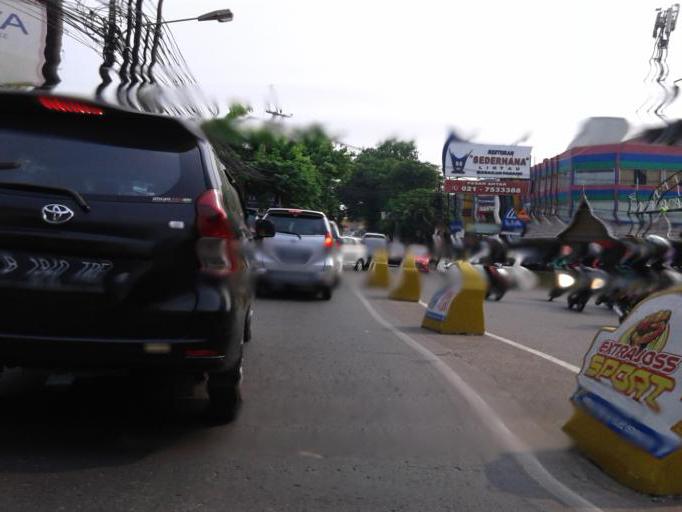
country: ID
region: West Java
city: Pamulang
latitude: -6.3329
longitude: 106.7830
